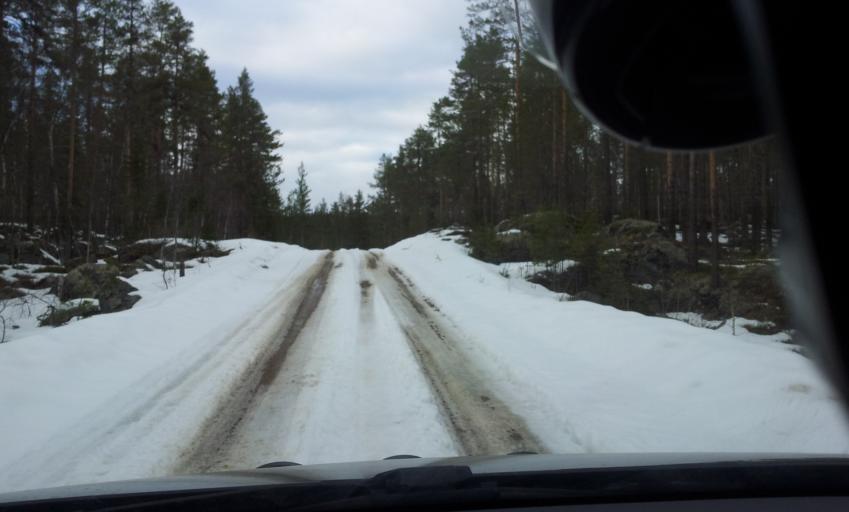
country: SE
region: Gaevleborg
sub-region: Ljusdals Kommun
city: Farila
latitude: 62.1654
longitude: 15.8273
